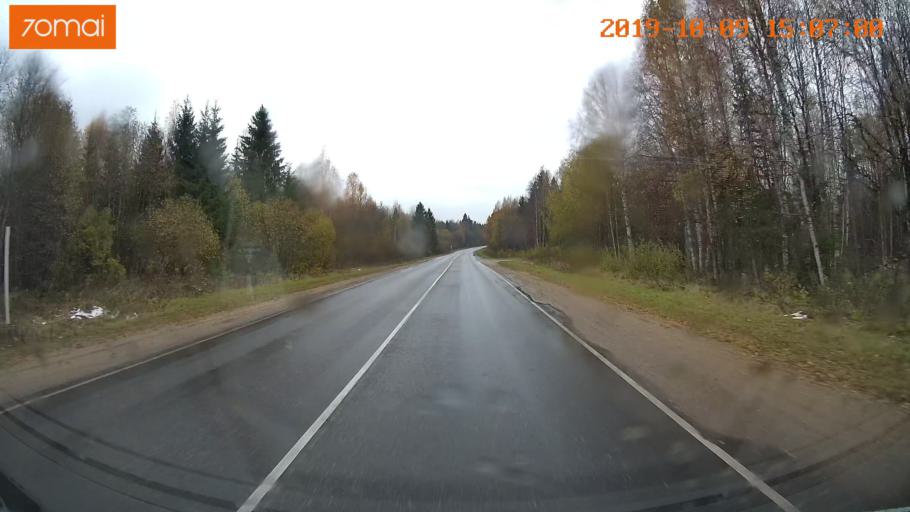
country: RU
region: Kostroma
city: Susanino
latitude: 58.2249
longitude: 41.6539
